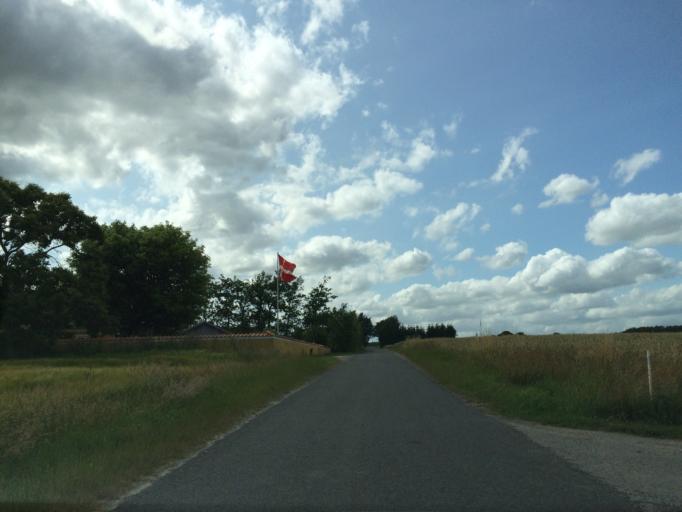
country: DK
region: Central Jutland
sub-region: Skanderborg Kommune
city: Galten
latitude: 56.1639
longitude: 9.8453
